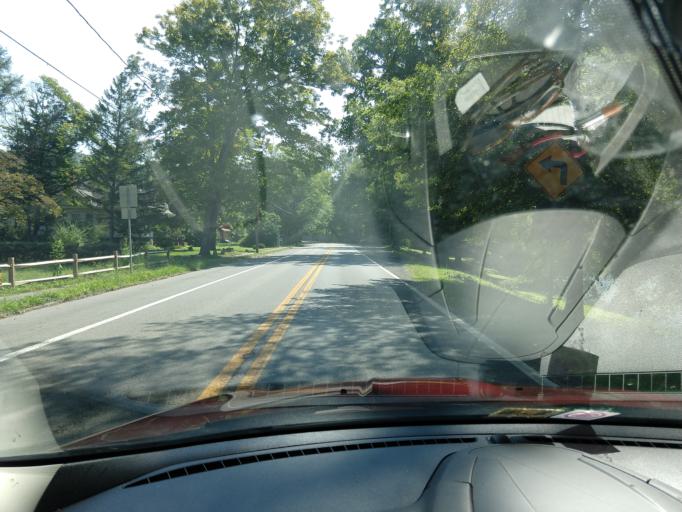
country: US
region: West Virginia
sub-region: Greenbrier County
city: Alderson
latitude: 37.7252
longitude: -80.6344
